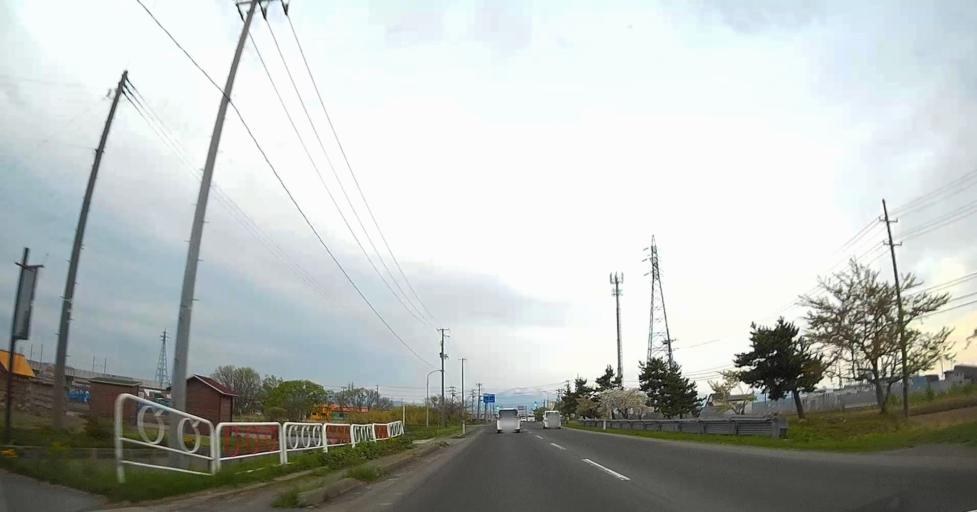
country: JP
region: Aomori
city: Aomori Shi
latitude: 40.8448
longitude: 140.6860
